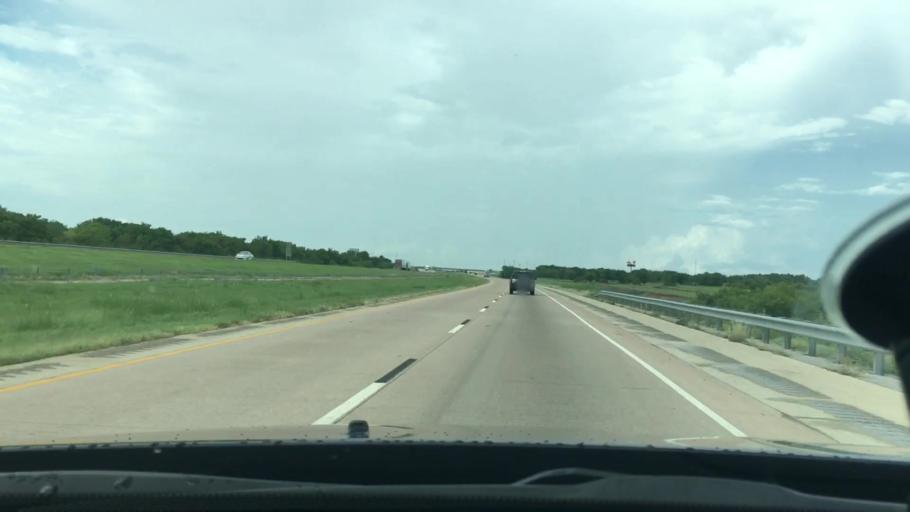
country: US
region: Oklahoma
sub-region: Garvin County
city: Pauls Valley
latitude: 34.6960
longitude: -97.2360
